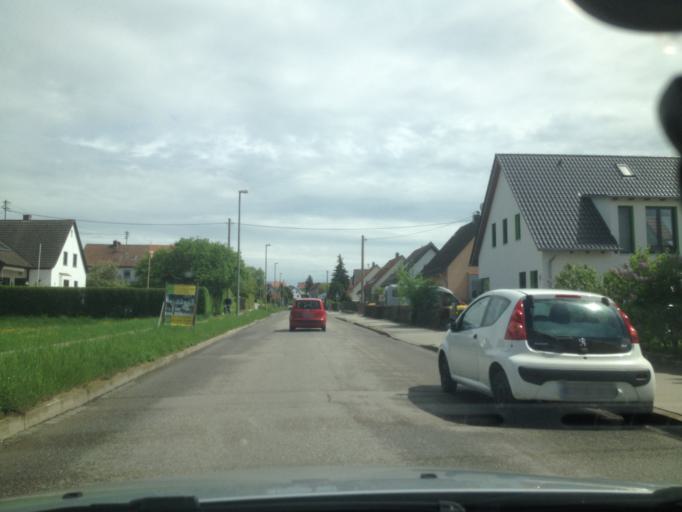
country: DE
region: Bavaria
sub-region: Swabia
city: Bobingen
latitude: 48.3141
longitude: 10.8511
